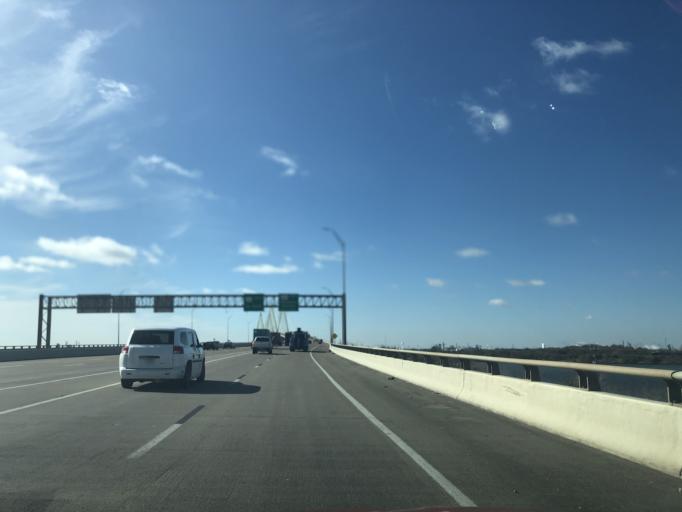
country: US
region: Texas
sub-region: Harris County
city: Baytown
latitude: 29.7130
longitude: -95.0031
